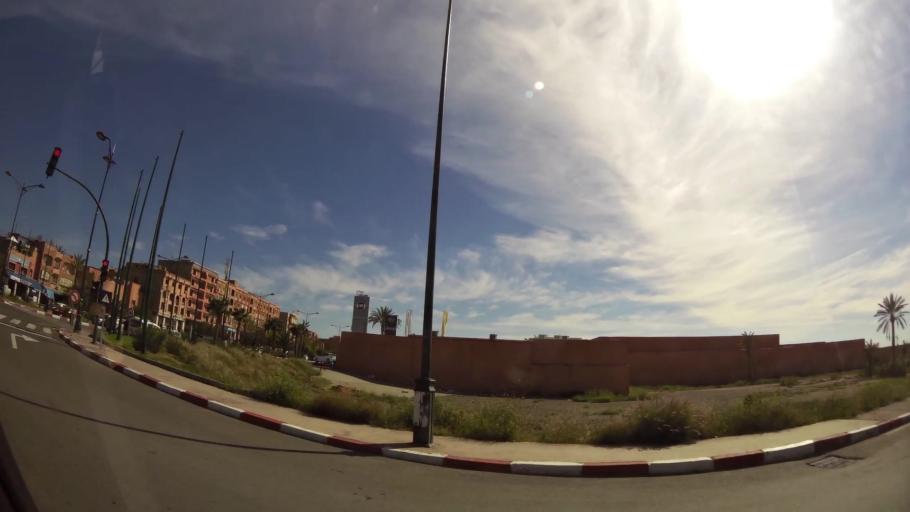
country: MA
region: Marrakech-Tensift-Al Haouz
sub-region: Marrakech
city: Marrakesh
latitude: 31.6583
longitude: -8.0176
